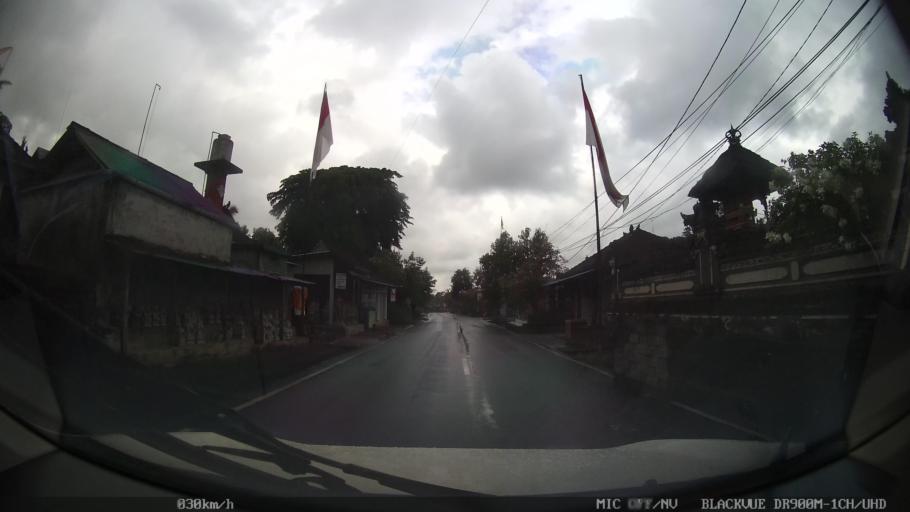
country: ID
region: Bali
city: Banjar Sayanbaleran
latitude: -8.5044
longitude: 115.1868
